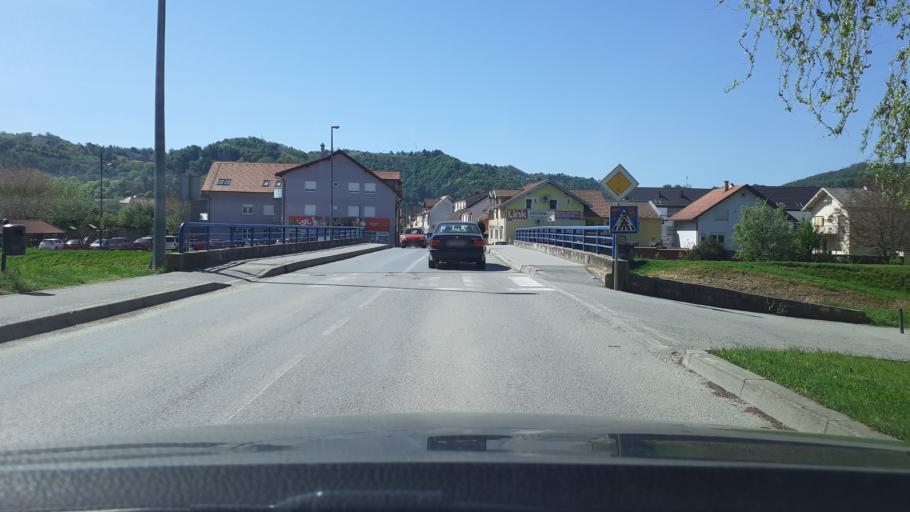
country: HR
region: Pozesko-Slavonska
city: Pozega
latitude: 45.3386
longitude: 17.6754
